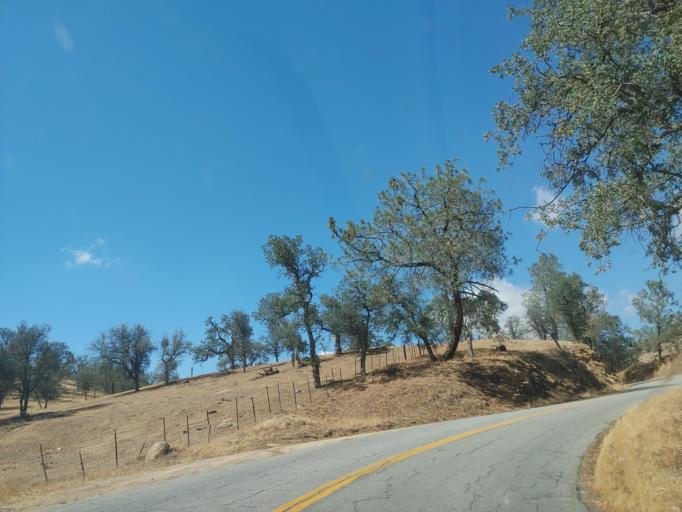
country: US
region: California
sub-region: Kern County
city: Golden Hills
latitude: 35.2100
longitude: -118.5521
